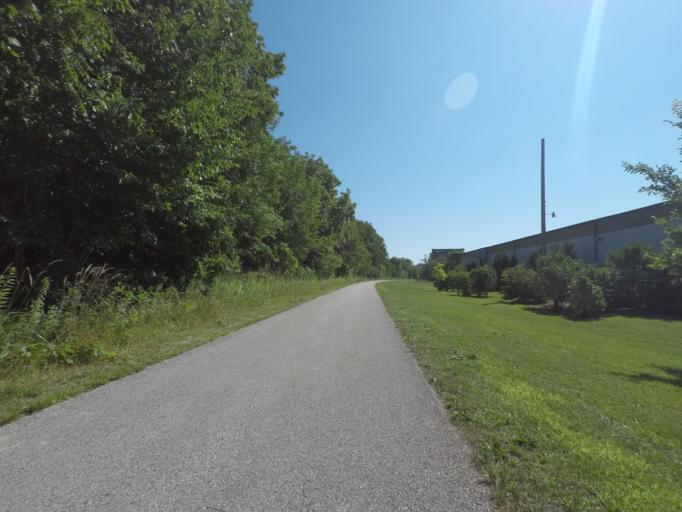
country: US
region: Wisconsin
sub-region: Milwaukee County
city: West Milwaukee
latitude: 43.0247
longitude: -87.9805
